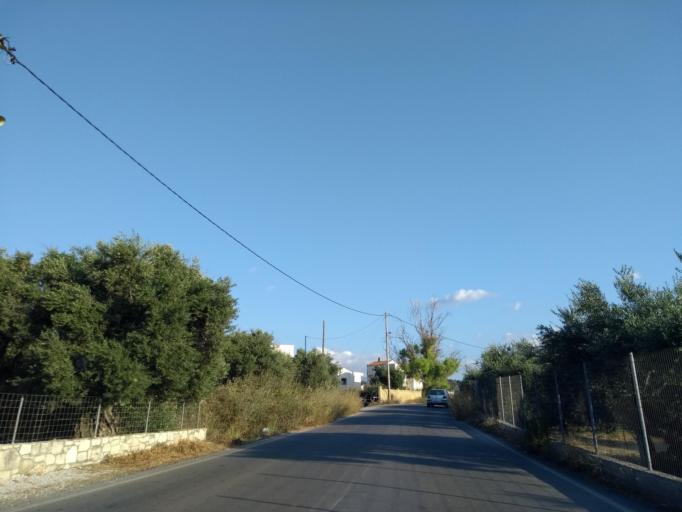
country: GR
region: Crete
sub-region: Nomos Chanias
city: Kalivai
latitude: 35.4441
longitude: 24.1760
